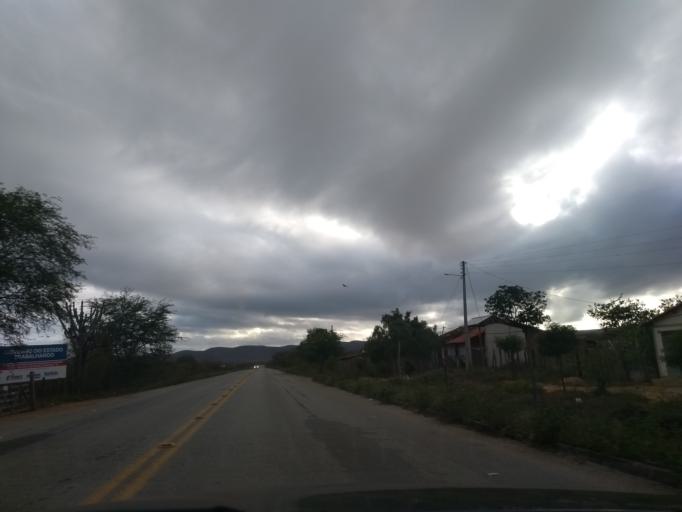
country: BR
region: Bahia
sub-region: Ituacu
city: Ituacu
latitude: -13.7589
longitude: -41.0312
